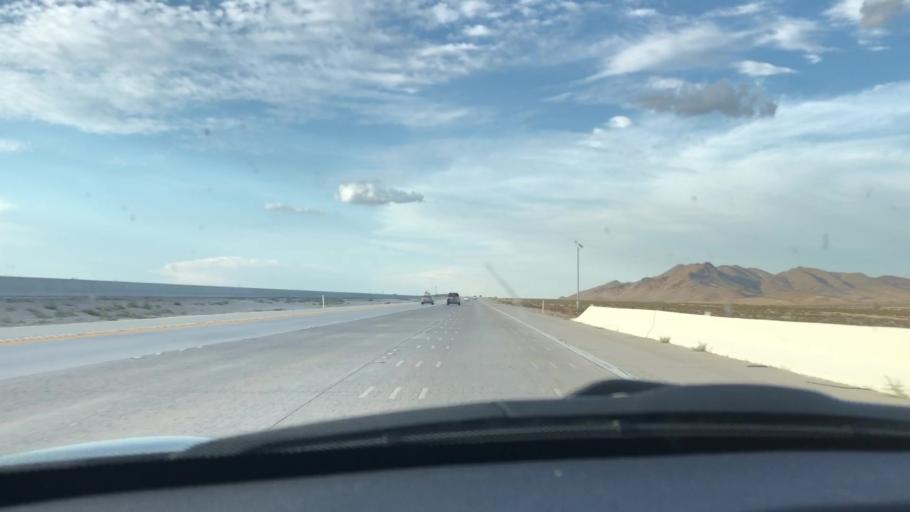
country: US
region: Nevada
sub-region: Clark County
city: Enterprise
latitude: 35.8675
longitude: -115.2465
